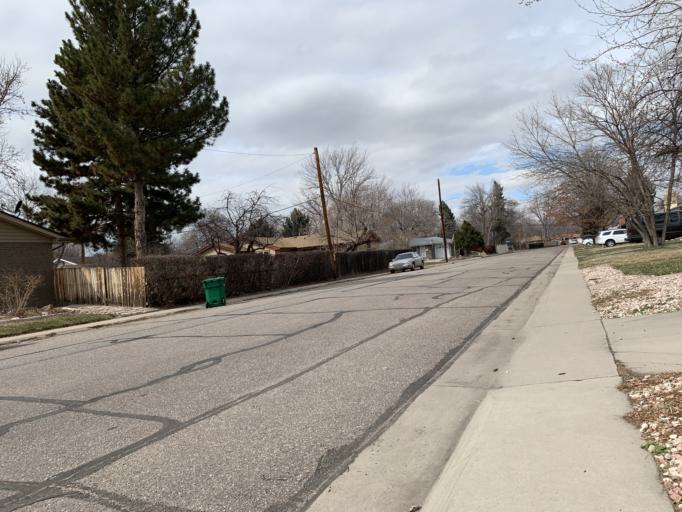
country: US
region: Colorado
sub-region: Arapahoe County
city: Columbine Valley
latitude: 39.6134
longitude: -105.0303
